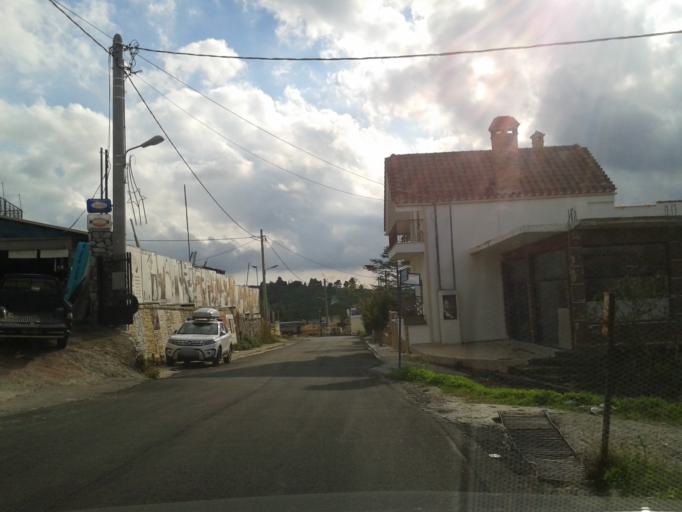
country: GR
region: Attica
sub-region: Nomarchia Anatolikis Attikis
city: Varnavas
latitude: 38.2224
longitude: 23.9245
